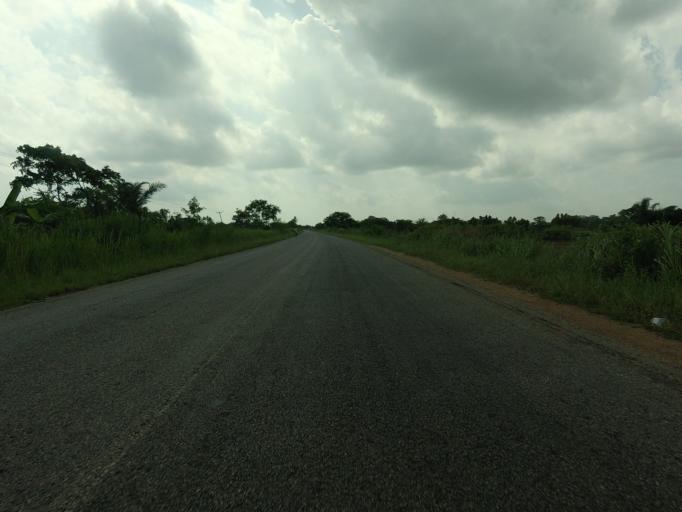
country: GH
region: Volta
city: Ho
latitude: 6.4338
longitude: 0.7316
